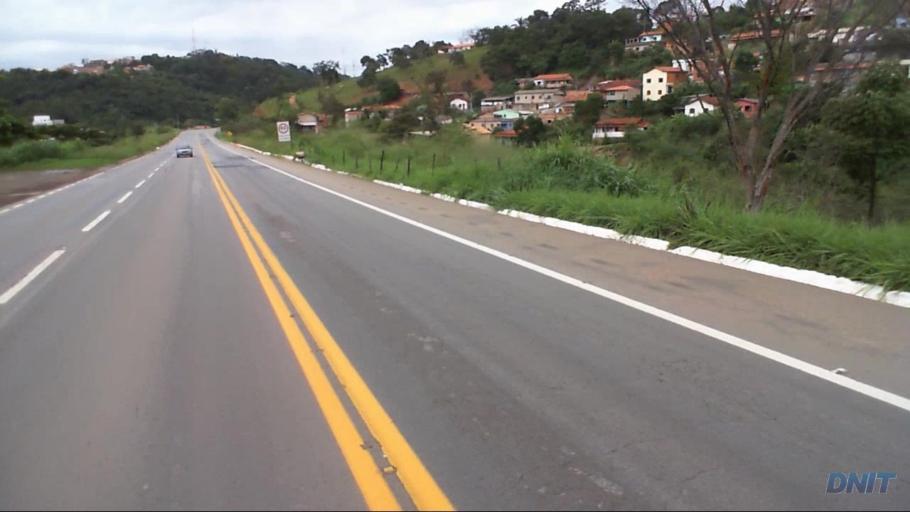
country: BR
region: Minas Gerais
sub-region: Barao De Cocais
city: Barao de Cocais
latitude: -19.8334
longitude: -43.3603
